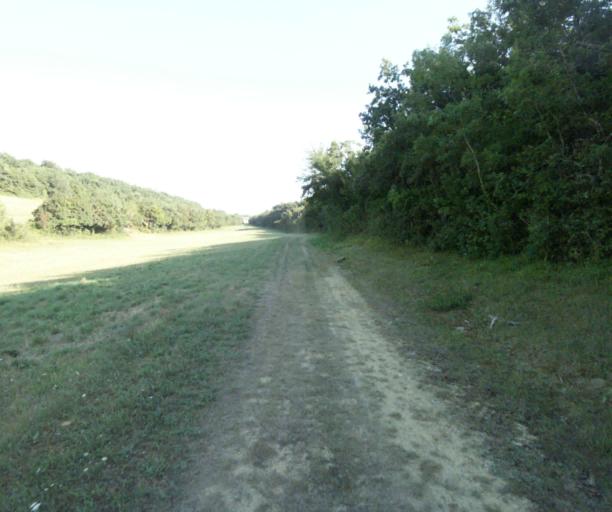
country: FR
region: Midi-Pyrenees
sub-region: Departement de la Haute-Garonne
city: Saint-Felix-Lauragais
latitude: 43.4378
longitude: 1.8203
